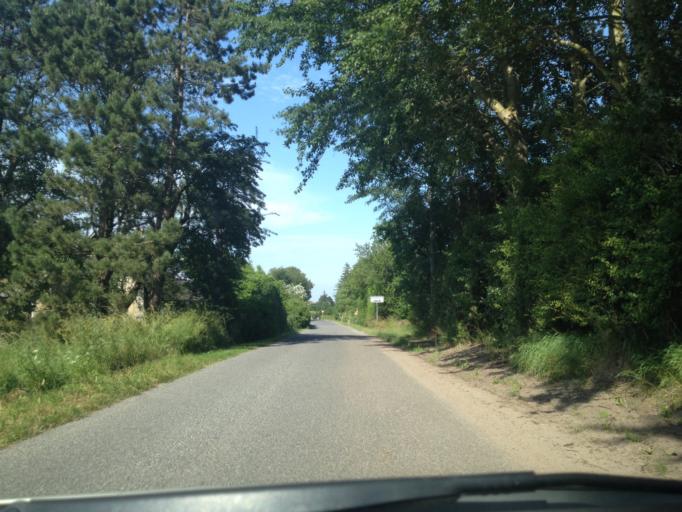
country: DK
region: Central Jutland
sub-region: Samso Kommune
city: Tranebjerg
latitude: 55.8456
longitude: 10.5635
